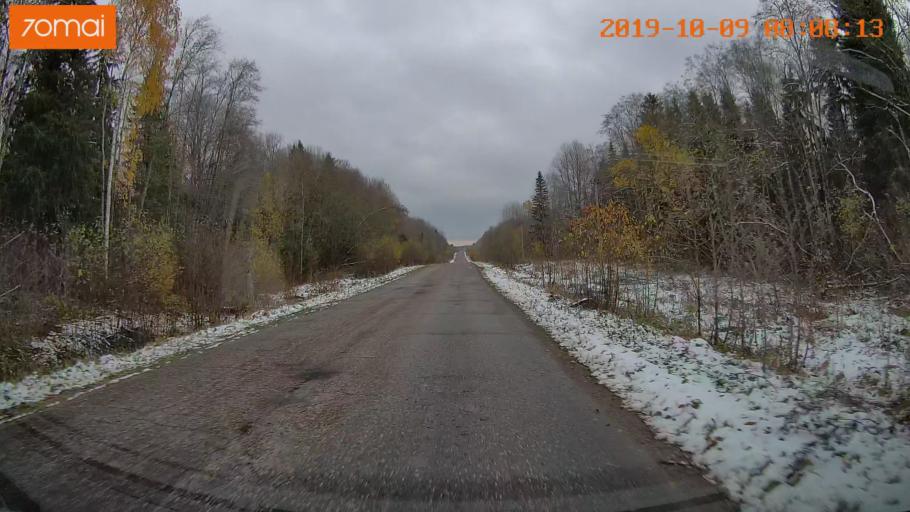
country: RU
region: Jaroslavl
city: Kukoboy
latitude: 58.7028
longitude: 40.0921
